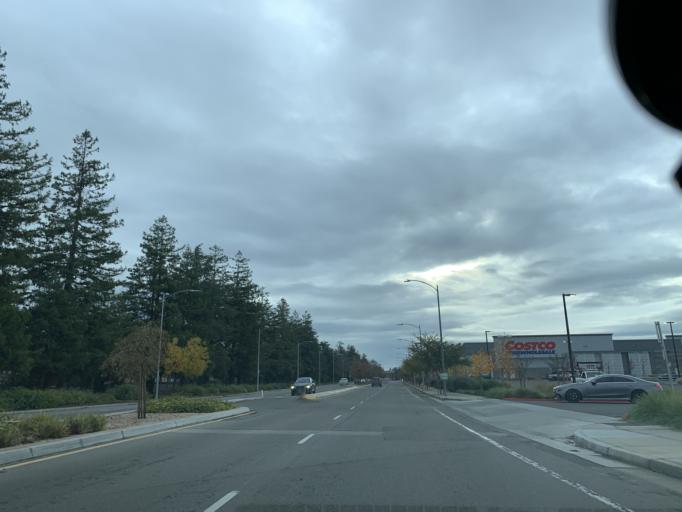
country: US
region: California
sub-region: Santa Clara County
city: Seven Trees
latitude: 37.2454
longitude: -121.7866
